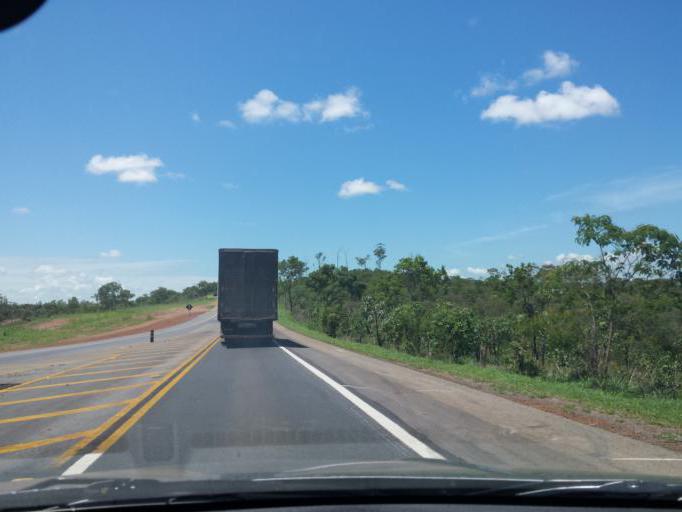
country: BR
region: Goias
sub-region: Luziania
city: Luziania
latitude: -16.5122
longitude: -47.8098
